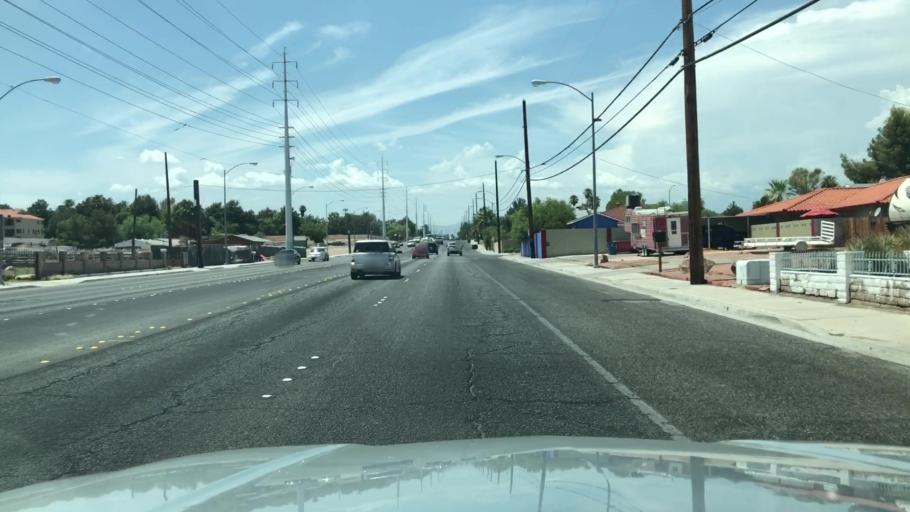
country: US
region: Nevada
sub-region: Clark County
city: Whitney
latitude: 36.0857
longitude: -115.0787
